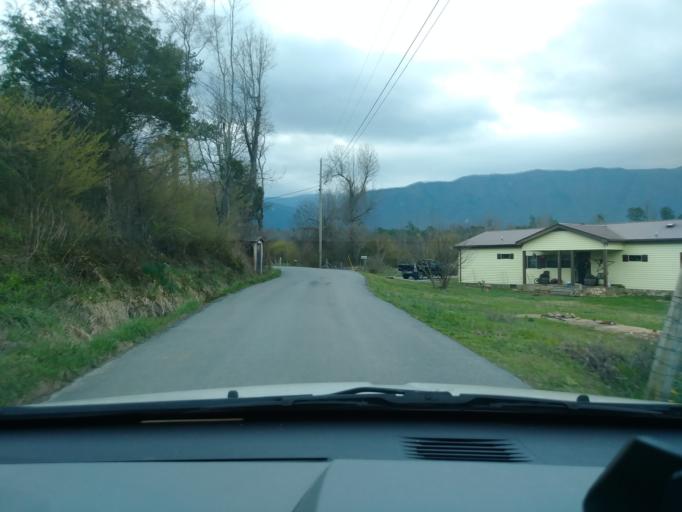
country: US
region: Tennessee
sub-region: Greene County
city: Tusculum
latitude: 36.0868
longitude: -82.7456
